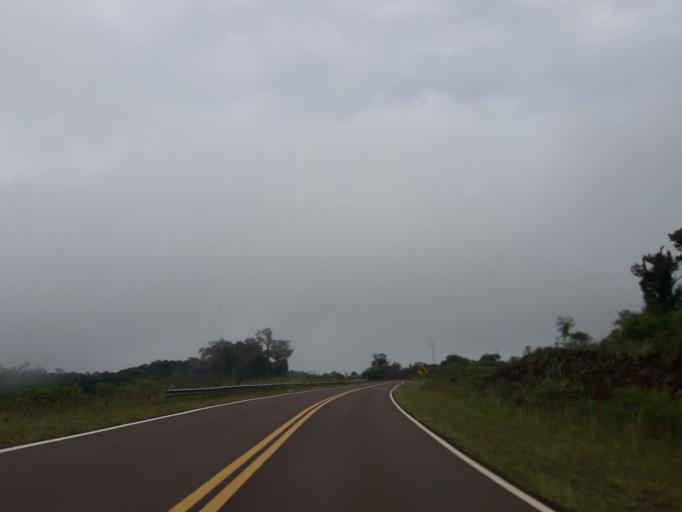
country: AR
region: Misiones
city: Bernardo de Irigoyen
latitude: -26.4067
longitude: -53.8220
